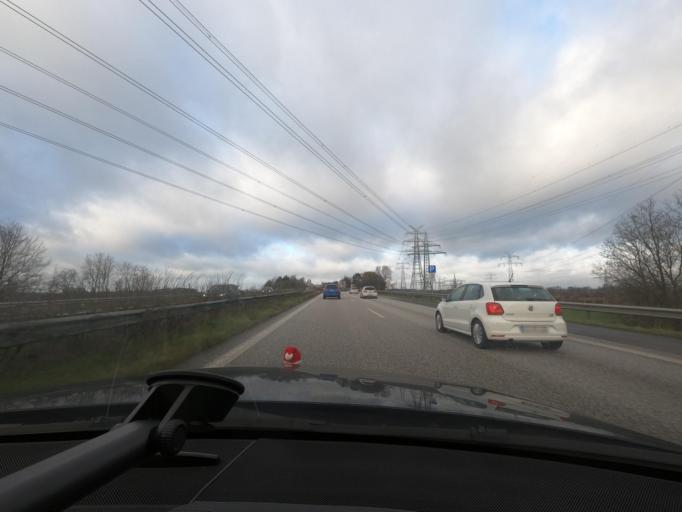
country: DE
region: Schleswig-Holstein
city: Schulldorf
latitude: 54.3195
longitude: 9.7417
